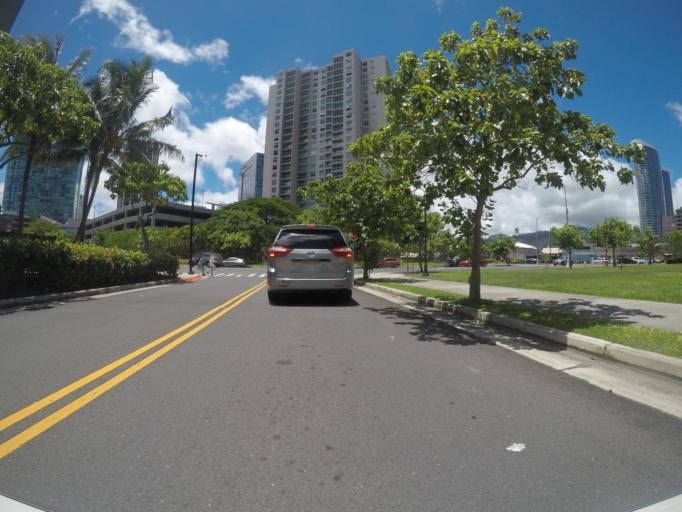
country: US
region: Hawaii
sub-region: Honolulu County
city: Honolulu
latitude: 21.2937
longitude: -157.8502
